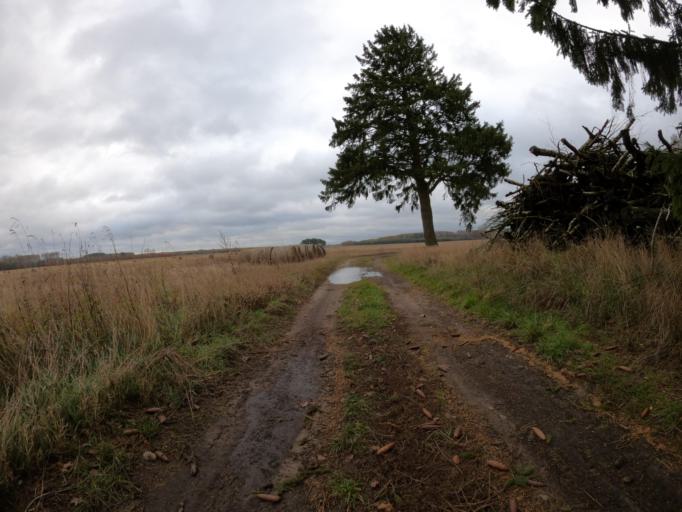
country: PL
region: West Pomeranian Voivodeship
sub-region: Powiat walecki
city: Miroslawiec
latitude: 53.3171
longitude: 16.1186
